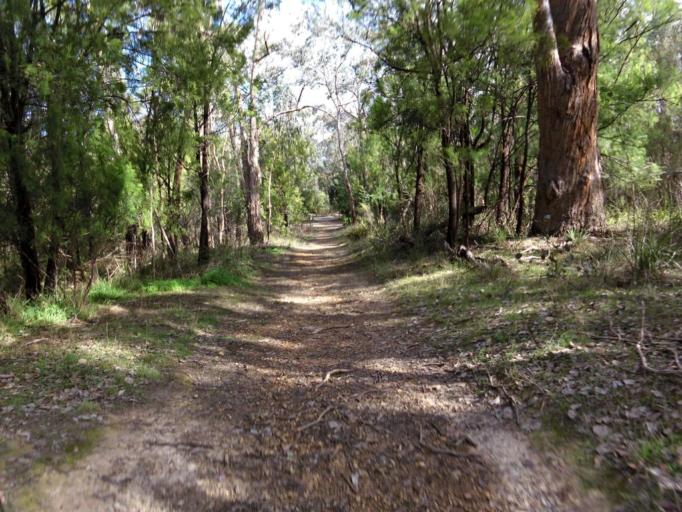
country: AU
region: Victoria
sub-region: Manningham
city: Park Orchards
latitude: -37.7765
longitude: 145.2258
